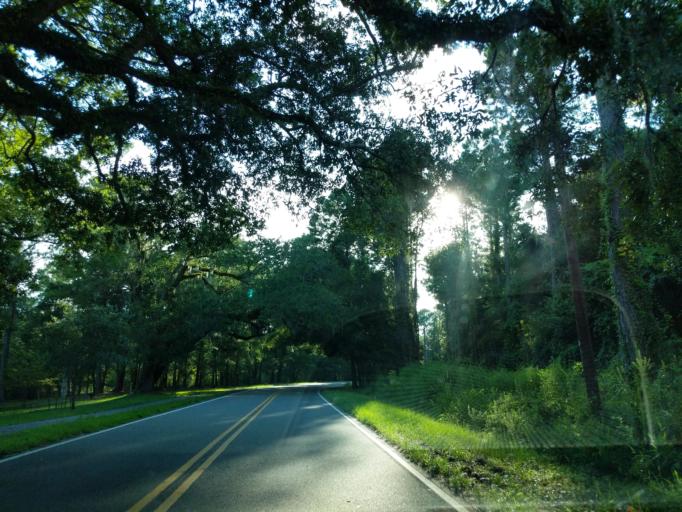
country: US
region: South Carolina
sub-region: Charleston County
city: Awendaw
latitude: 33.0923
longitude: -79.4725
